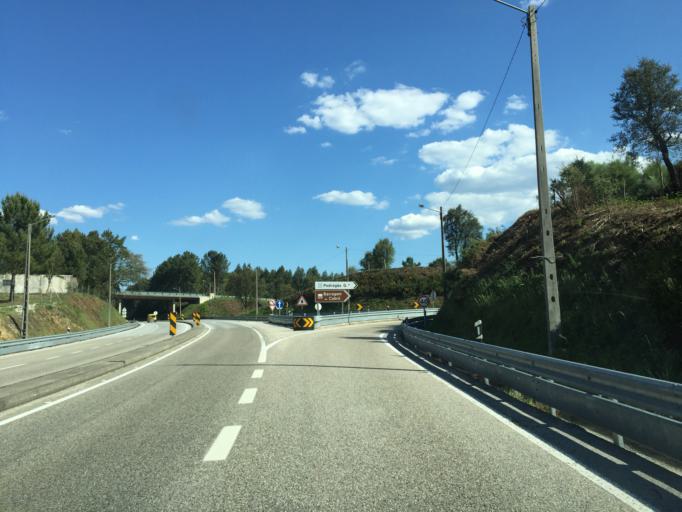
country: PT
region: Leiria
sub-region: Pedrogao Grande
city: Pedrogao Grande
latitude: 39.9108
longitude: -8.1529
